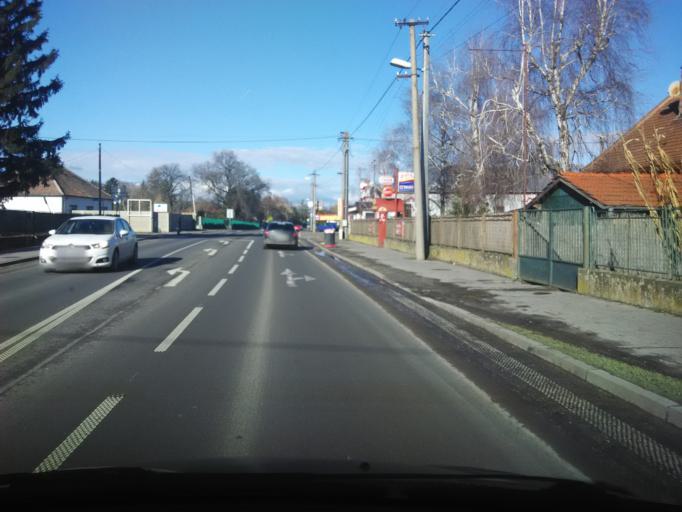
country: SK
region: Nitriansky
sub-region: Okres Nitra
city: Nitra
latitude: 48.2414
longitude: 18.1162
